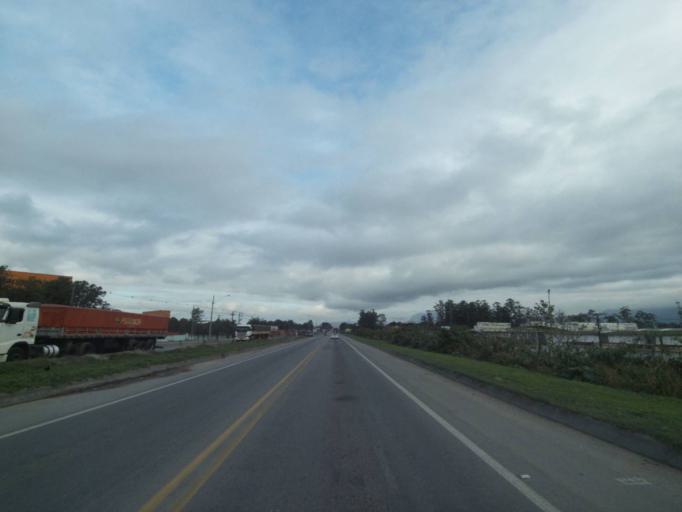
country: BR
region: Parana
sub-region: Paranagua
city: Paranagua
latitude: -25.5413
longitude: -48.5589
